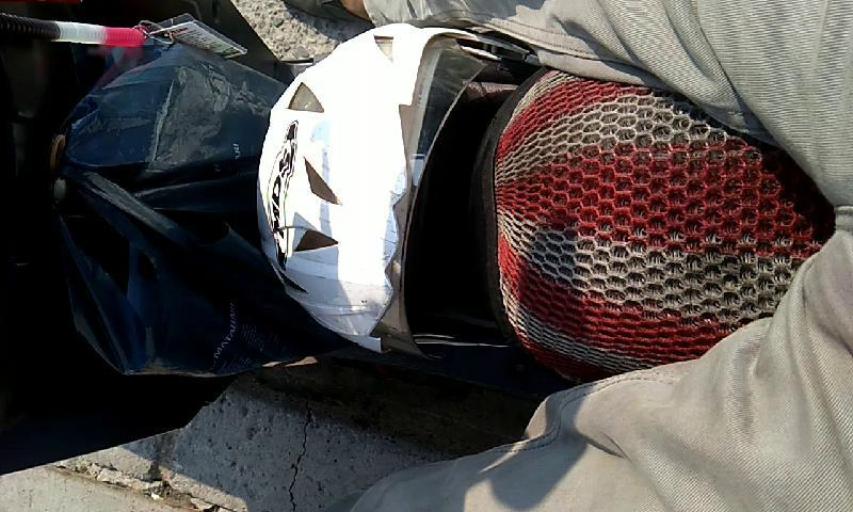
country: ID
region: West Java
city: Bekasi
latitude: -6.1547
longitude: 106.9711
